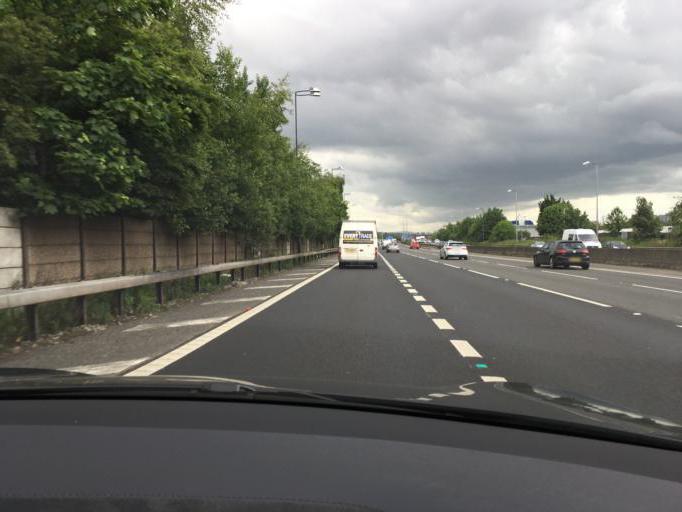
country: GB
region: England
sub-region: Borough of Stockport
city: Cheadle Heath
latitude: 53.4078
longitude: -2.1854
